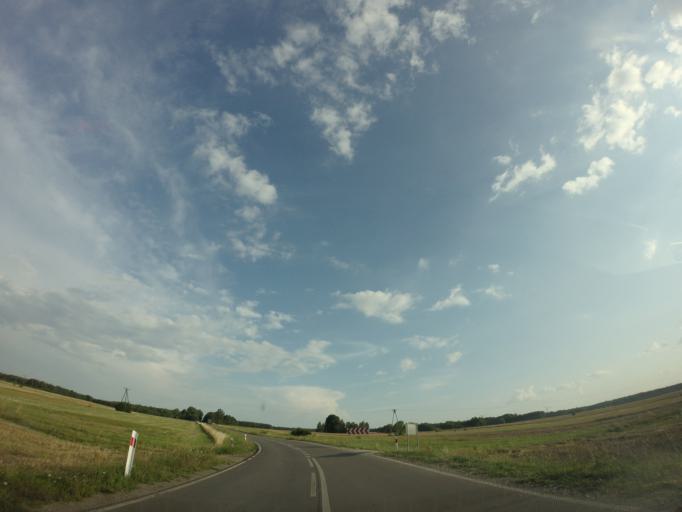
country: PL
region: Lublin Voivodeship
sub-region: Powiat lubartowski
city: Michow
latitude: 51.5480
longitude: 22.2995
